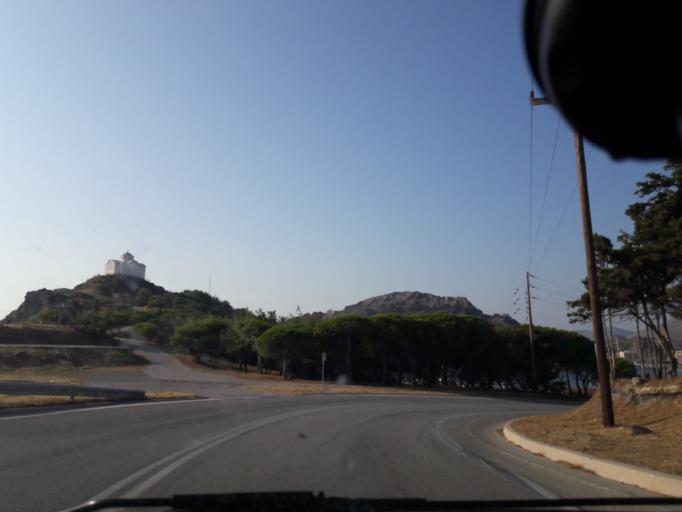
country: GR
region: North Aegean
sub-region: Nomos Lesvou
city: Myrina
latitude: 39.8677
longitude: 25.0555
